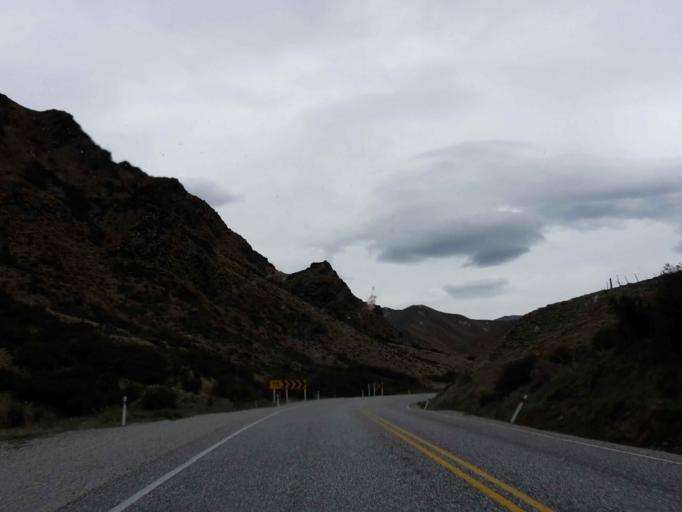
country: NZ
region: Otago
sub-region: Queenstown-Lakes District
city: Wanaka
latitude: -44.5799
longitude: 169.6061
